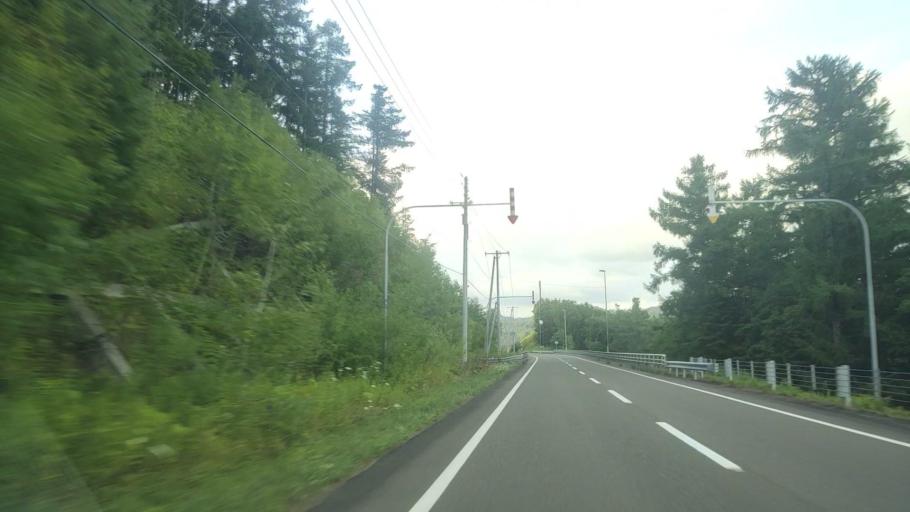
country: JP
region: Hokkaido
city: Bibai
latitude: 43.0669
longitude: 142.1025
